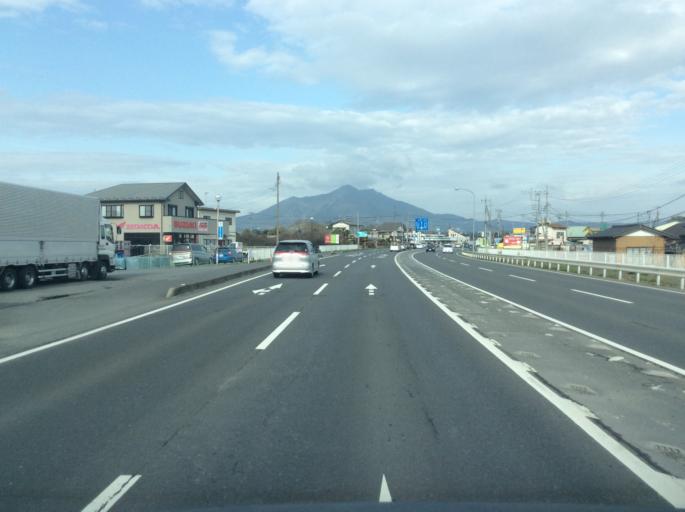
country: JP
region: Ibaraki
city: Ishige
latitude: 36.1898
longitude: 140.0129
